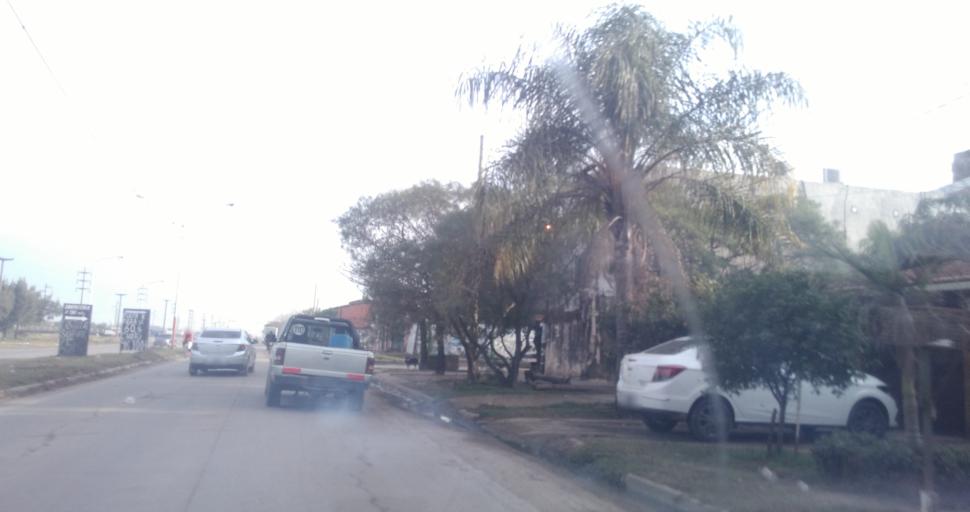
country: AR
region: Chaco
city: Resistencia
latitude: -27.4786
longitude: -58.9986
